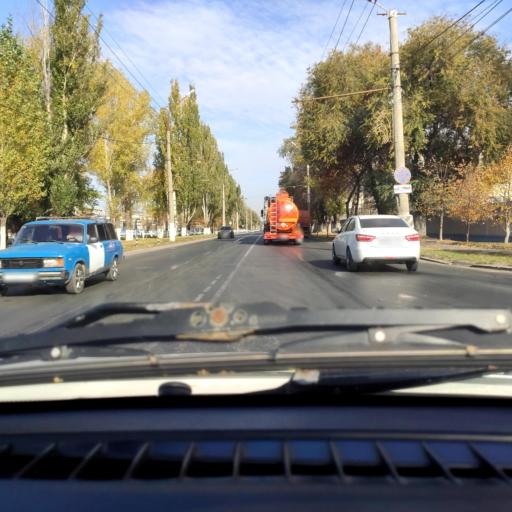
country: RU
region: Samara
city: Tol'yatti
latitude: 53.5521
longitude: 49.4495
